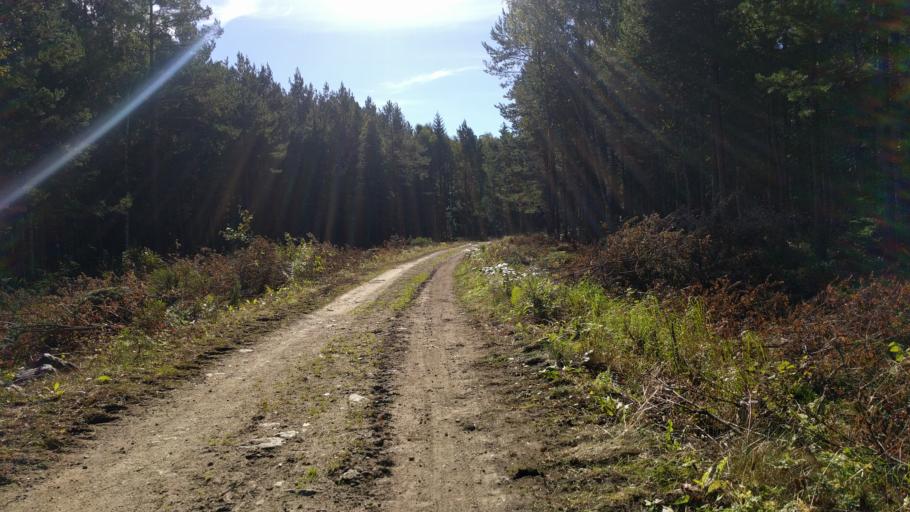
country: SE
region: Stockholm
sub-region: Vallentuna Kommun
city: Vallentuna
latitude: 59.4941
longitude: 18.1122
